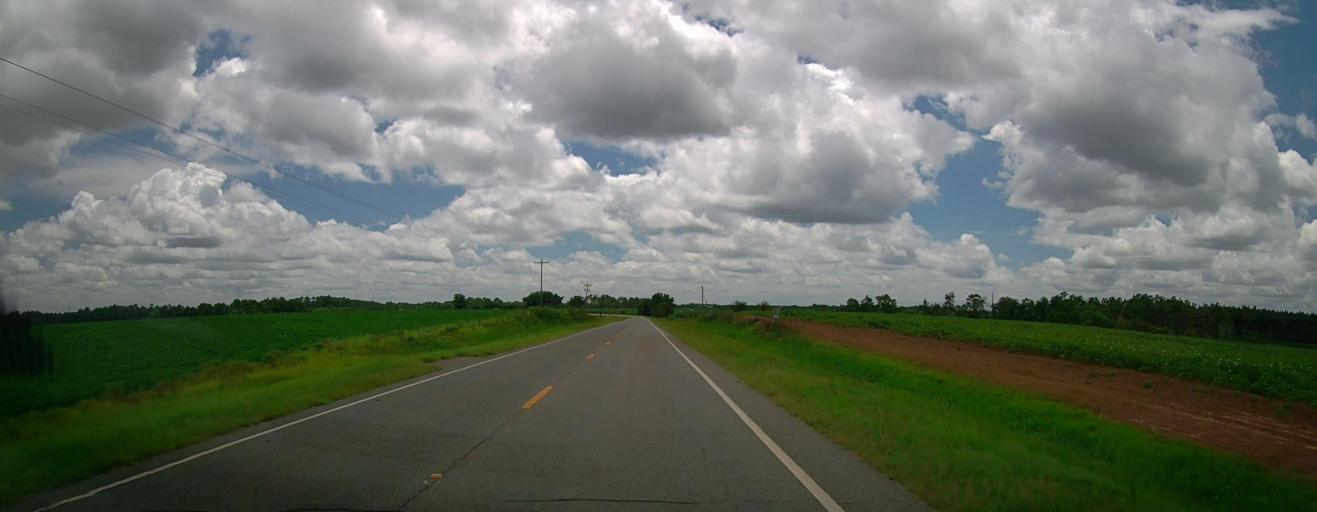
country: US
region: Georgia
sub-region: Wilcox County
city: Rochelle
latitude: 31.9743
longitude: -83.5467
